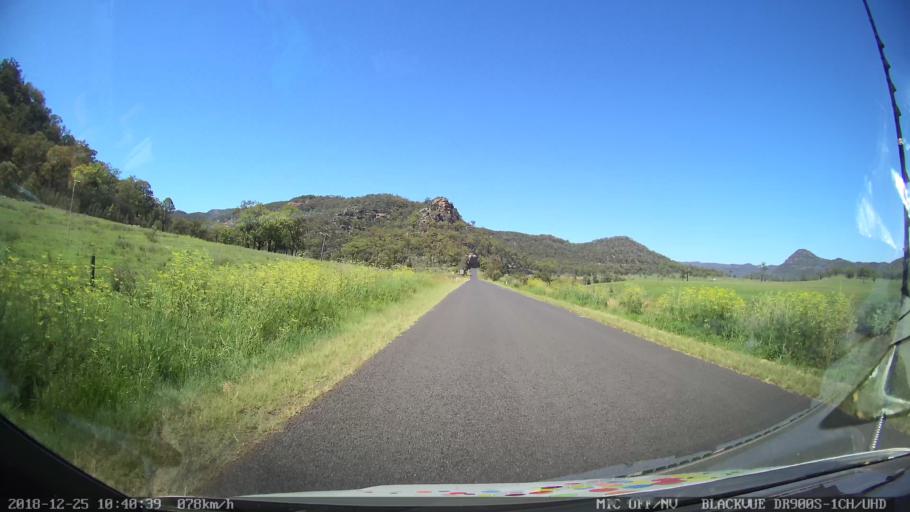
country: AU
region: New South Wales
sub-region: Upper Hunter Shire
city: Merriwa
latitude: -32.4097
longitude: 150.3417
